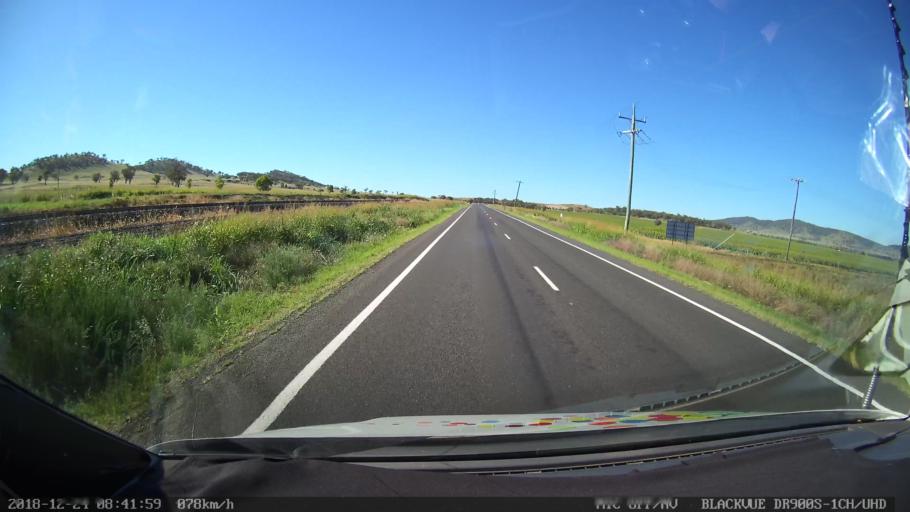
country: AU
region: New South Wales
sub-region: Liverpool Plains
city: Quirindi
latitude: -31.3685
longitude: 150.6438
